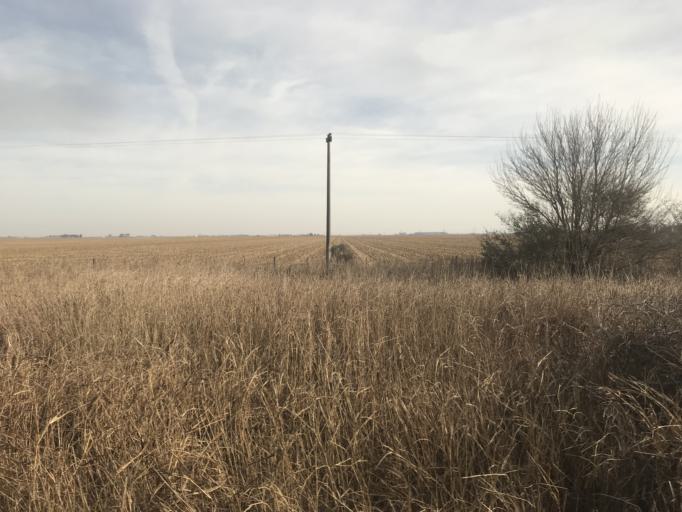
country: AR
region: Cordoba
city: Pilar
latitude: -31.7189
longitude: -63.8537
